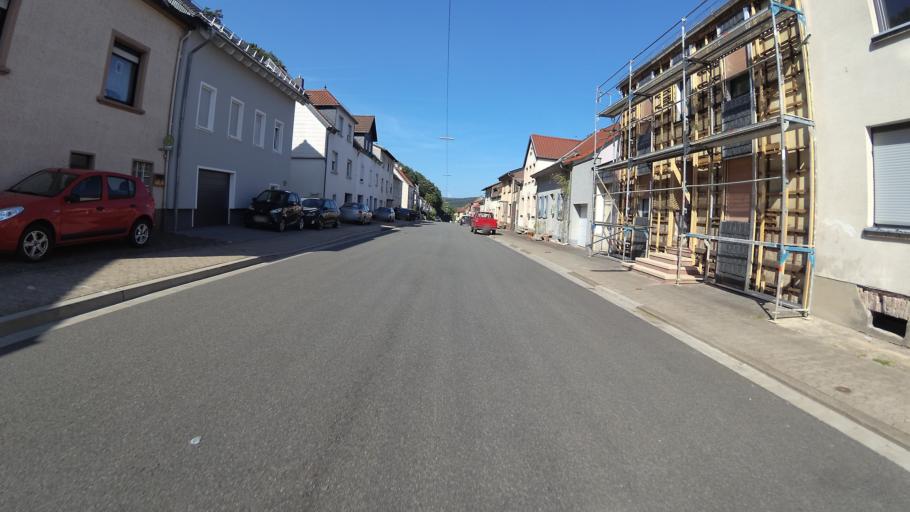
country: DE
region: Saarland
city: Eppelborn
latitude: 49.3965
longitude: 6.9619
